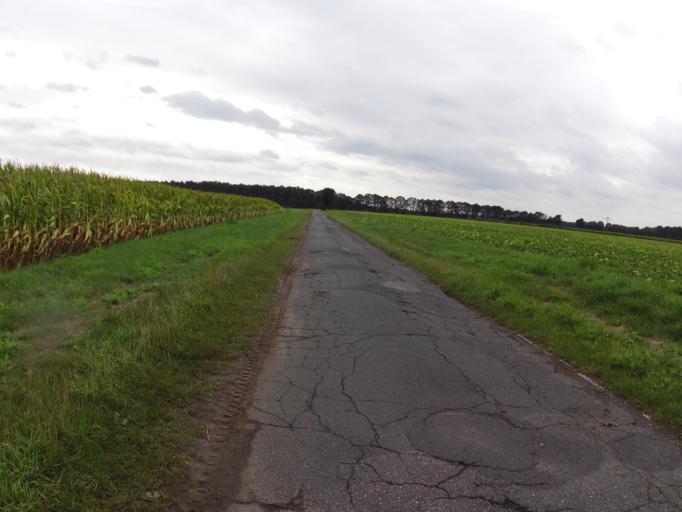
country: DE
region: Lower Saxony
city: Scheessel
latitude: 53.1521
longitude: 9.4523
